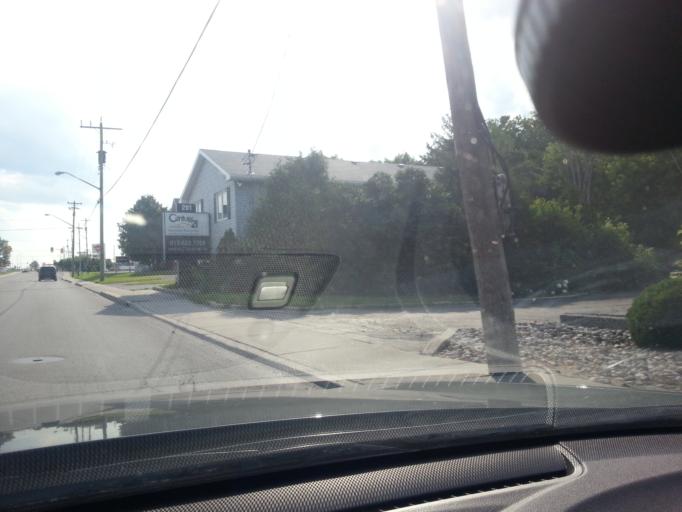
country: CA
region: Ontario
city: Arnprior
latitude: 45.4264
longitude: -76.3632
